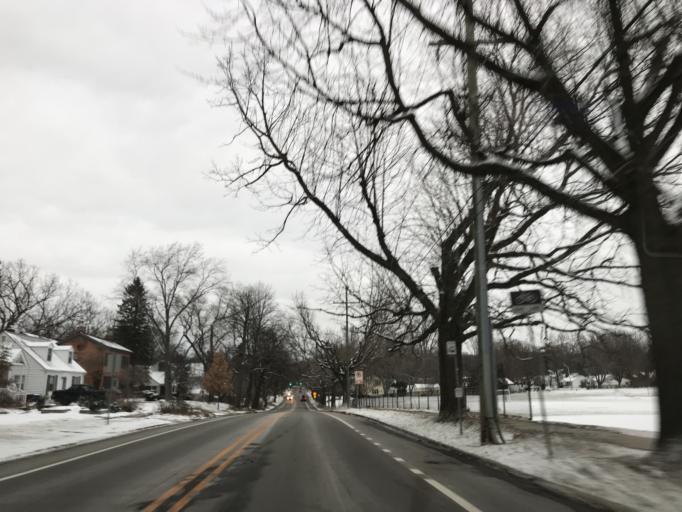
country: US
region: Michigan
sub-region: Washtenaw County
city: Ann Arbor
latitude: 42.2978
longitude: -83.7368
